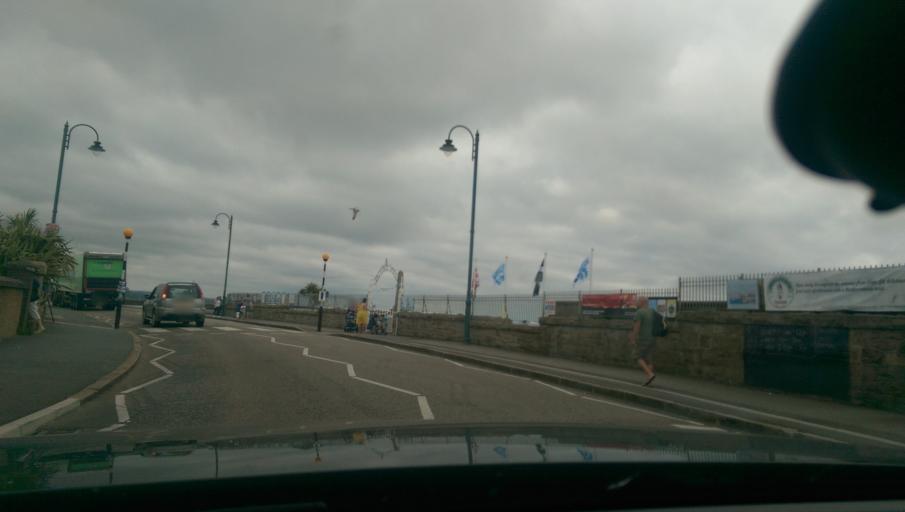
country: GB
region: England
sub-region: Cornwall
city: Penzance
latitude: 50.1153
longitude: -5.5325
